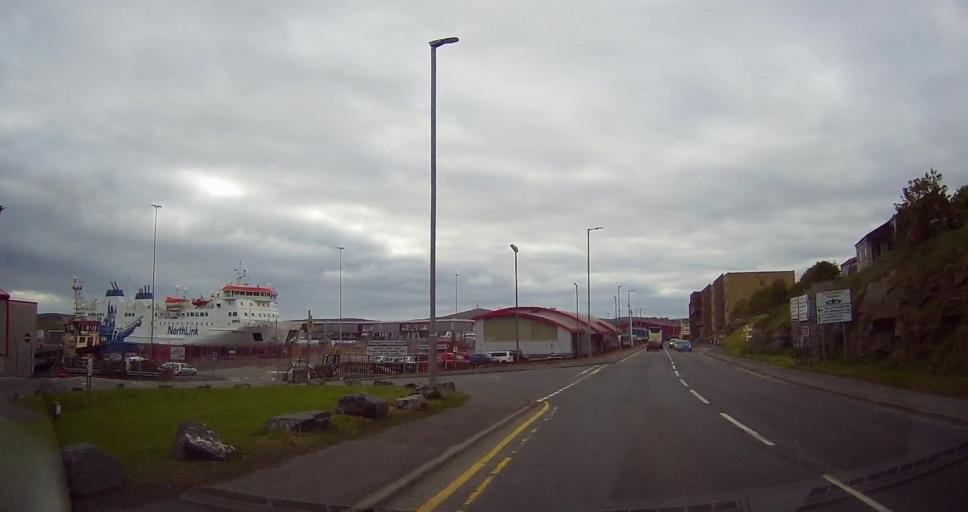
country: GB
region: Scotland
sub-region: Shetland Islands
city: Lerwick
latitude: 60.1637
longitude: -1.1606
